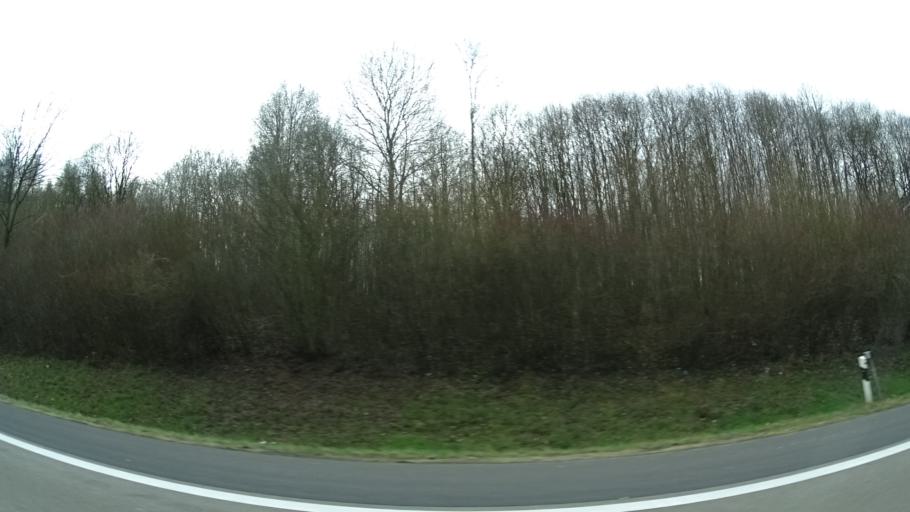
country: DE
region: Hesse
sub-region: Regierungsbezirk Darmstadt
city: Echzell
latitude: 50.3919
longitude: 8.9342
